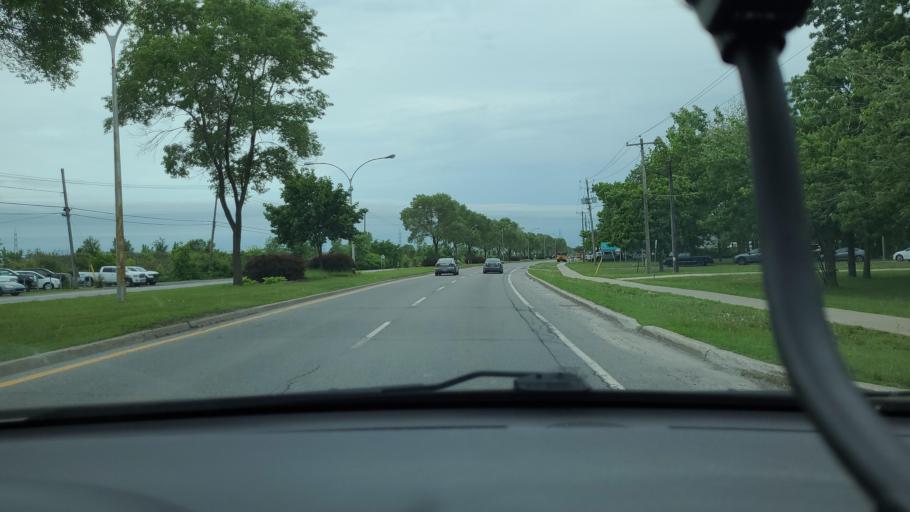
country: CA
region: Quebec
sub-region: Monteregie
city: La Prairie
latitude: 45.4034
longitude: -73.4998
